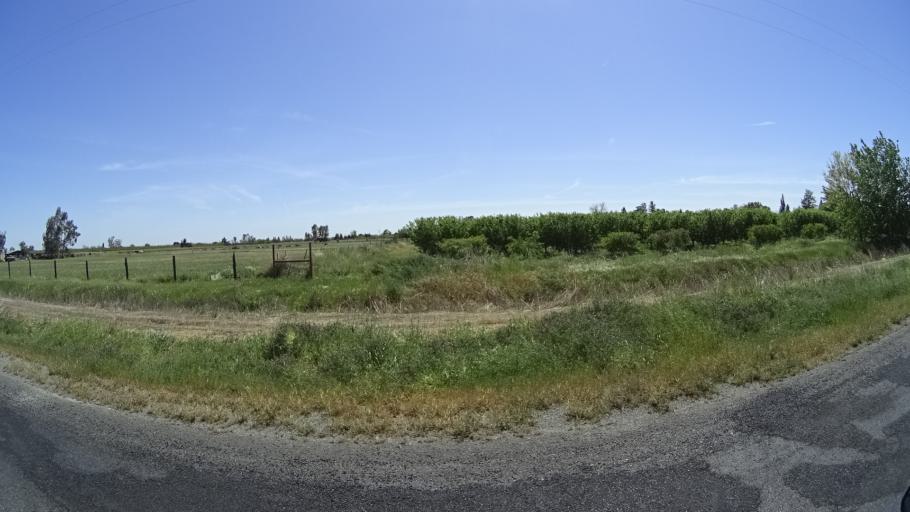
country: US
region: California
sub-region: Glenn County
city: Orland
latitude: 39.7398
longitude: -122.1572
